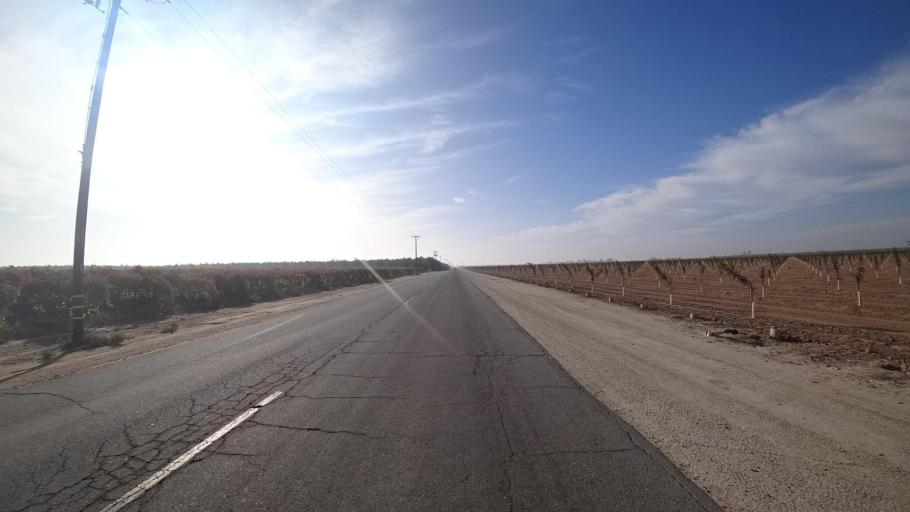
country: US
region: California
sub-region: Kern County
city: McFarland
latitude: 35.6588
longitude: -119.2046
